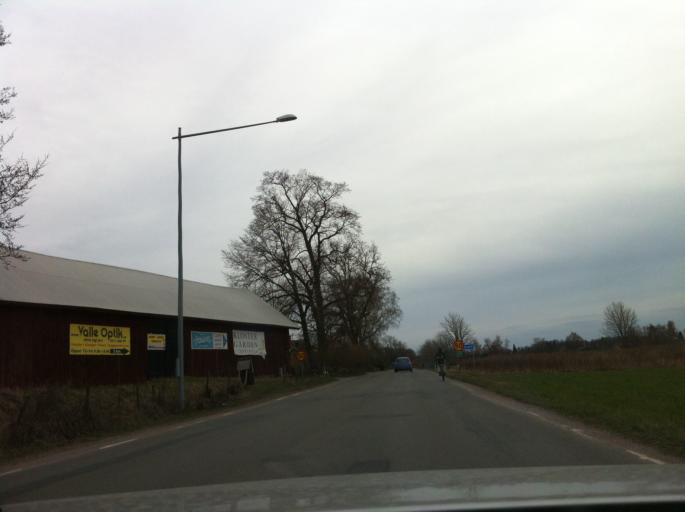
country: SE
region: Vaestra Goetaland
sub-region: Skara Kommun
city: Axvall
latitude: 58.3894
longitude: 13.6506
